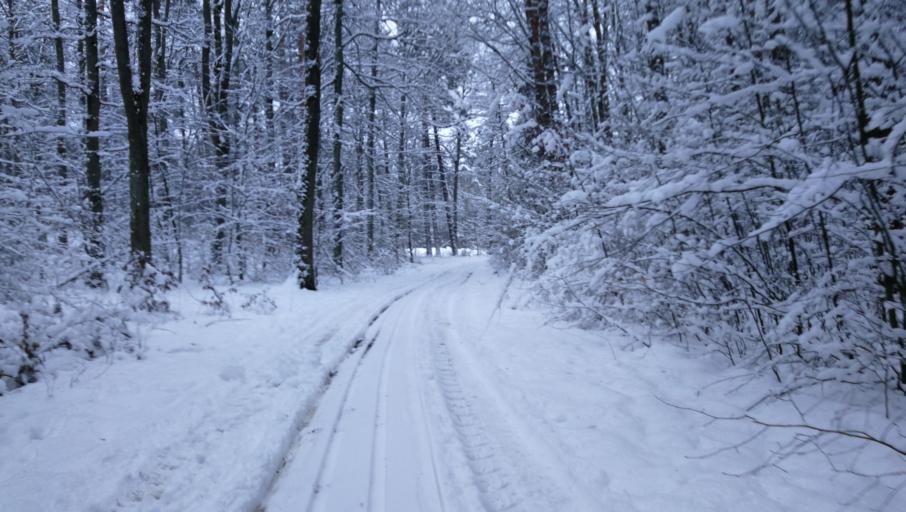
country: PL
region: Kujawsko-Pomorskie
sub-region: Powiat brodnicki
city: Gorzno
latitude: 53.2028
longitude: 19.6976
